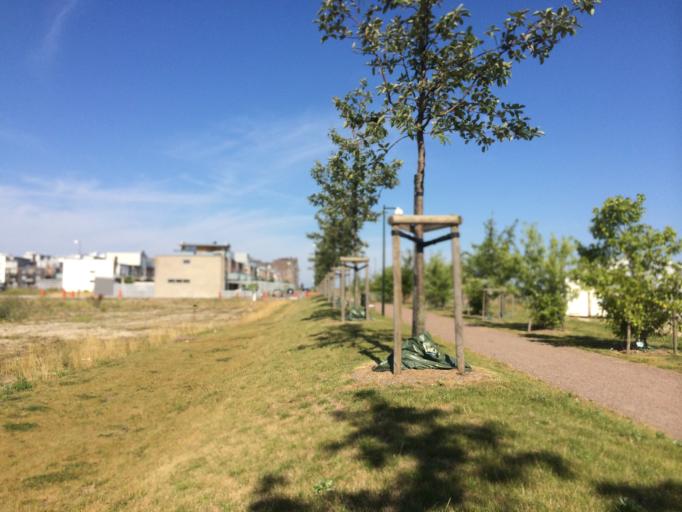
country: SE
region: Skane
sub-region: Malmo
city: Bunkeflostrand
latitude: 55.5912
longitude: 12.9362
